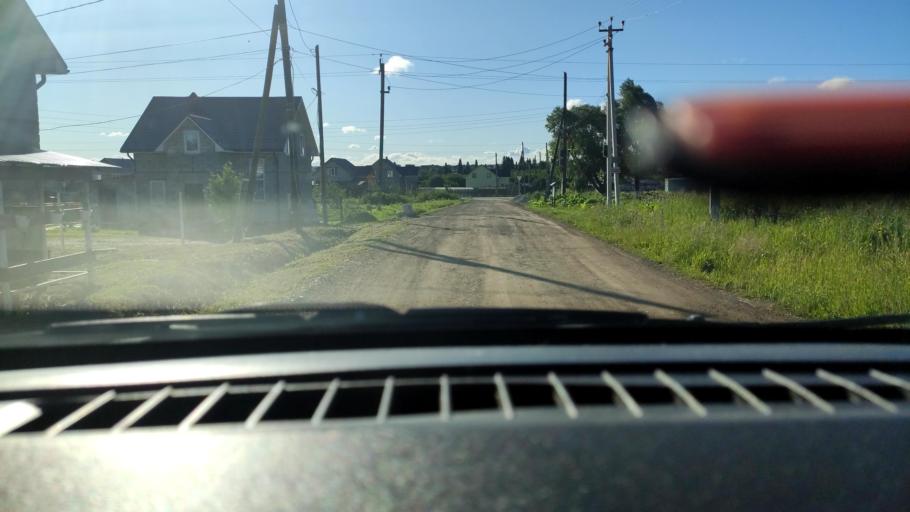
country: RU
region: Perm
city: Kultayevo
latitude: 57.8619
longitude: 55.9117
